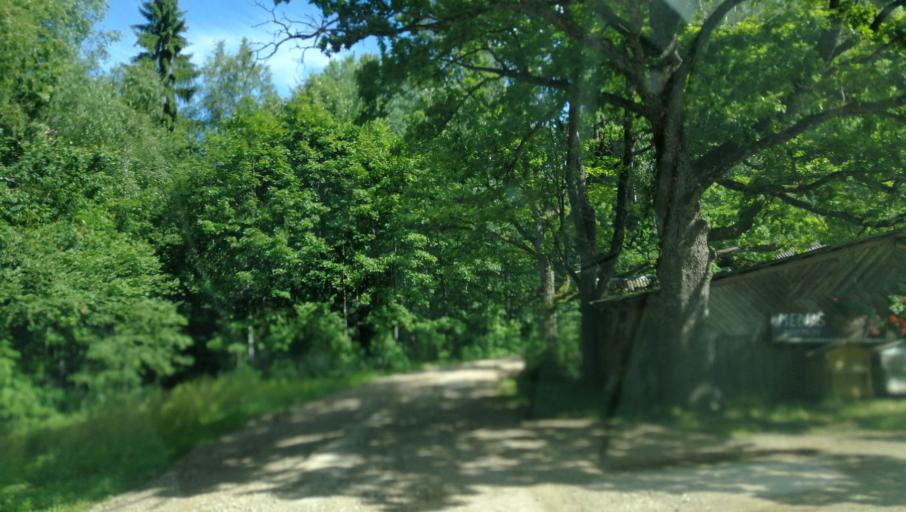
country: LV
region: Gulbenes Rajons
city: Gulbene
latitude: 57.1713
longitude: 26.8659
